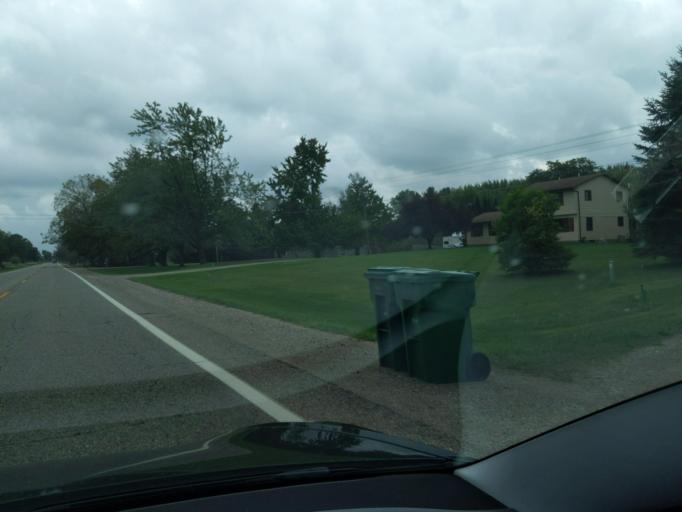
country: US
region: Michigan
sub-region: Eaton County
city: Potterville
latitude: 42.5514
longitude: -84.7564
